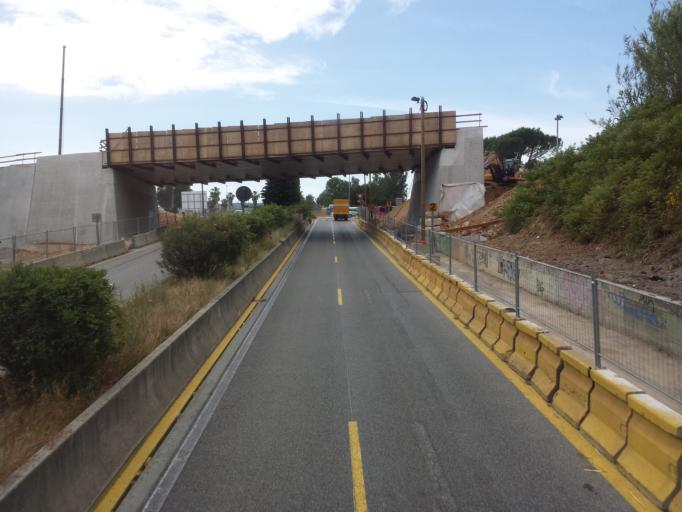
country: FR
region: Provence-Alpes-Cote d'Azur
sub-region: Departement des Alpes-Maritimes
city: Biot
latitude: 43.6056
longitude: 7.0817
